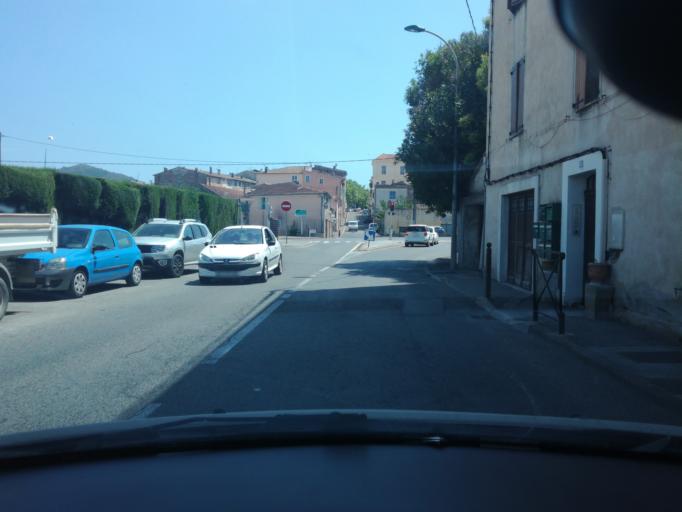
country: FR
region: Provence-Alpes-Cote d'Azur
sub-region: Departement du Var
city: Le Muy
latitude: 43.4753
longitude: 6.5667
